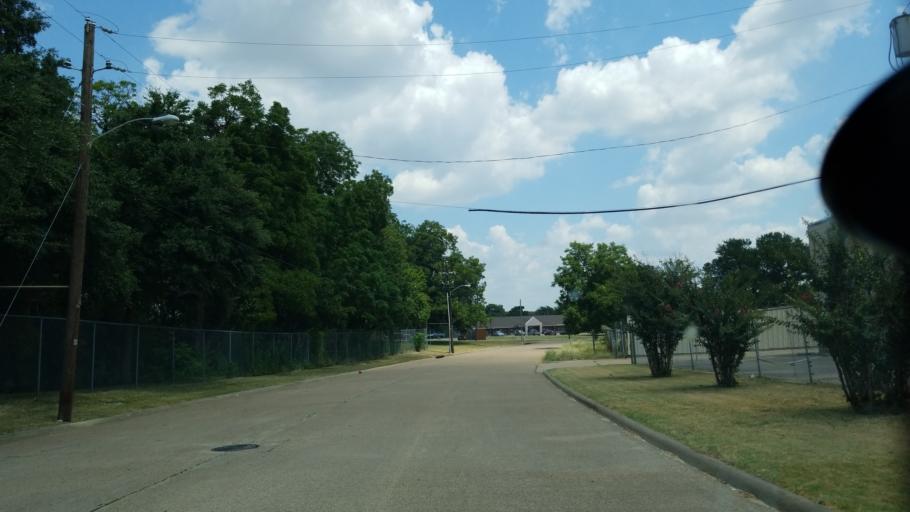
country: US
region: Texas
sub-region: Dallas County
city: Duncanville
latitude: 32.6882
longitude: -96.8845
